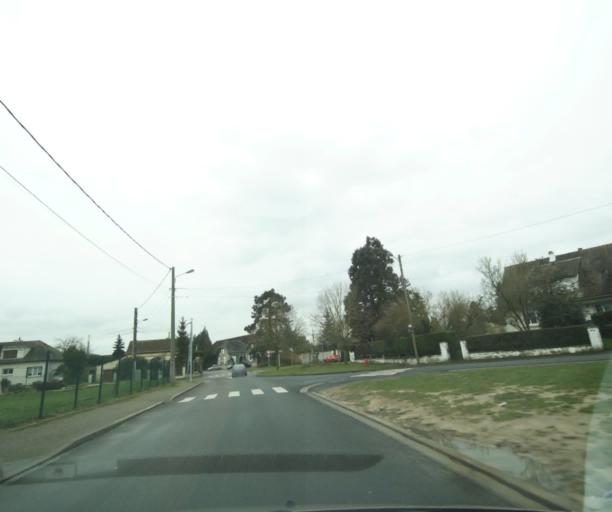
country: FR
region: Picardie
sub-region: Departement de l'Oise
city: Noyon
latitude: 49.5748
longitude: 2.9942
